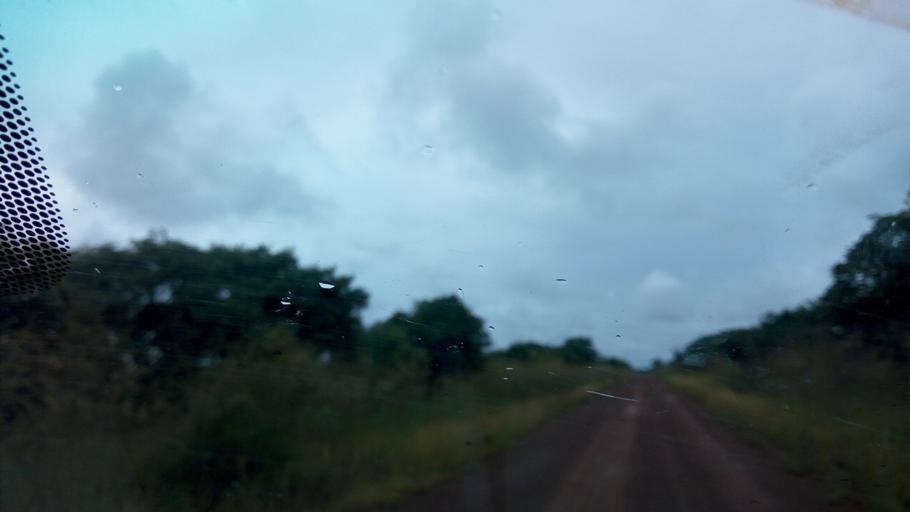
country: ZM
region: Luapula
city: Nchelenge
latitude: -9.0081
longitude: 28.4219
